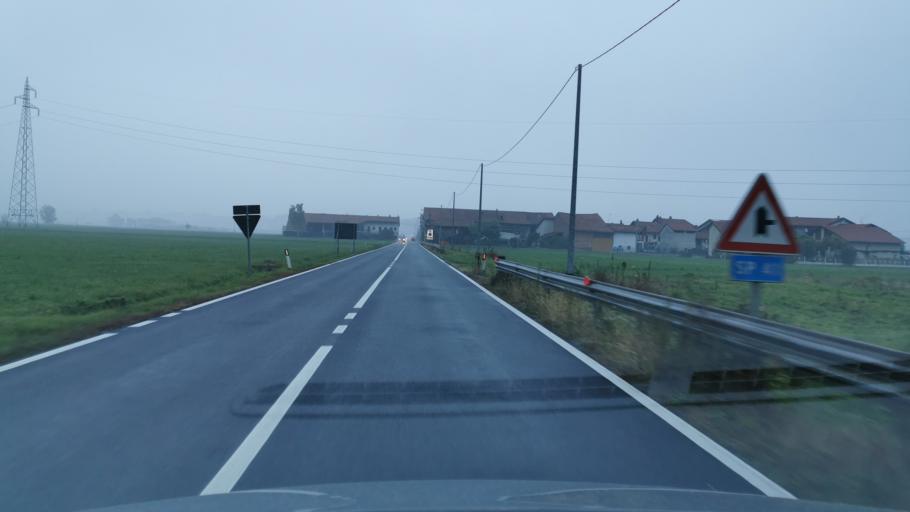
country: IT
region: Piedmont
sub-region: Provincia di Torino
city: Ciconio
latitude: 45.3455
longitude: 7.7656
